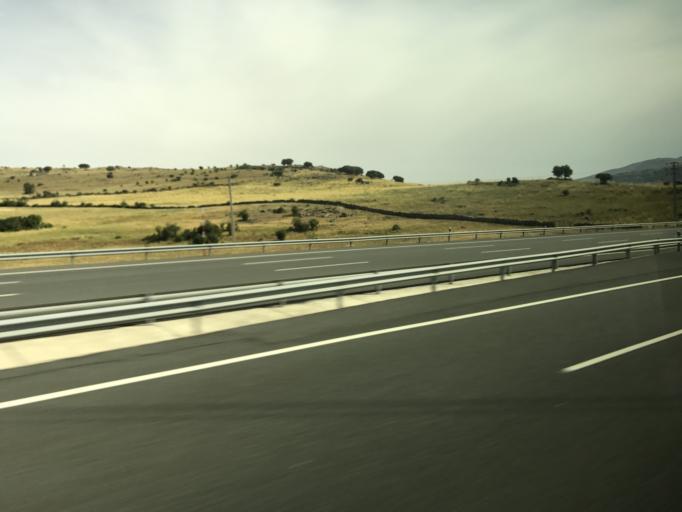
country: ES
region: Castille and Leon
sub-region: Provincia de Segovia
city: Vegas de Matute
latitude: 40.7397
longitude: -4.2591
